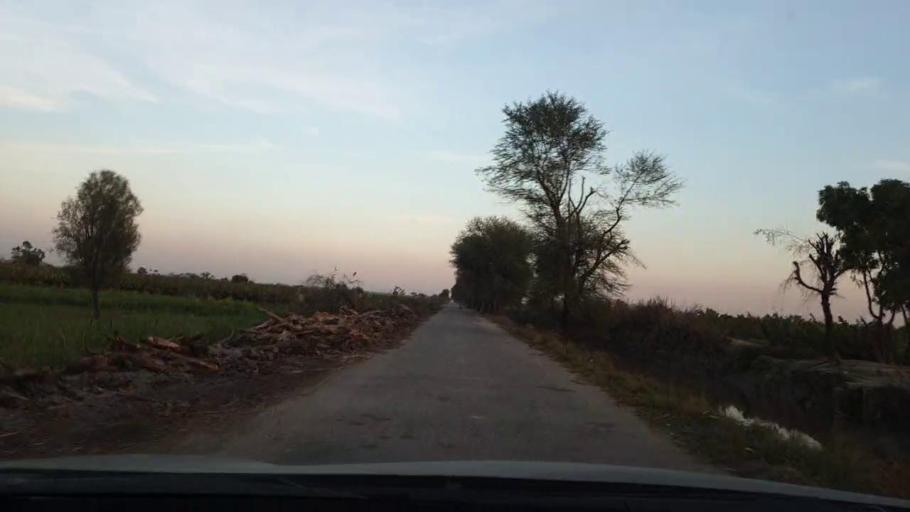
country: PK
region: Sindh
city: Tando Allahyar
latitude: 25.5954
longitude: 68.7041
